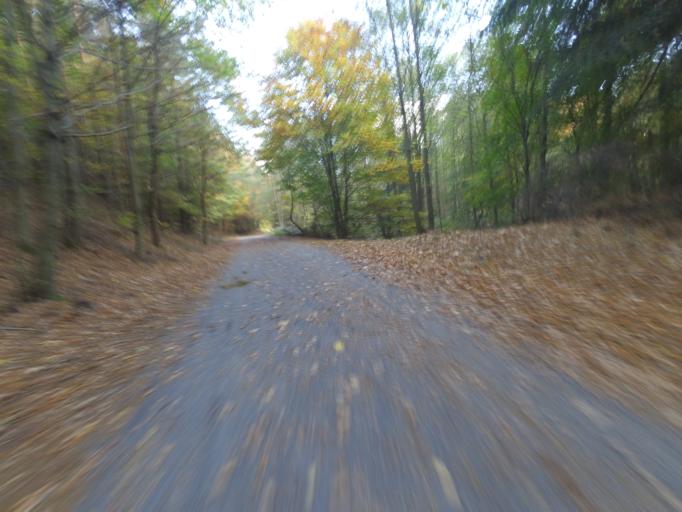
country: DE
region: Saxony
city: Albertstadt
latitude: 51.0948
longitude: 13.8368
